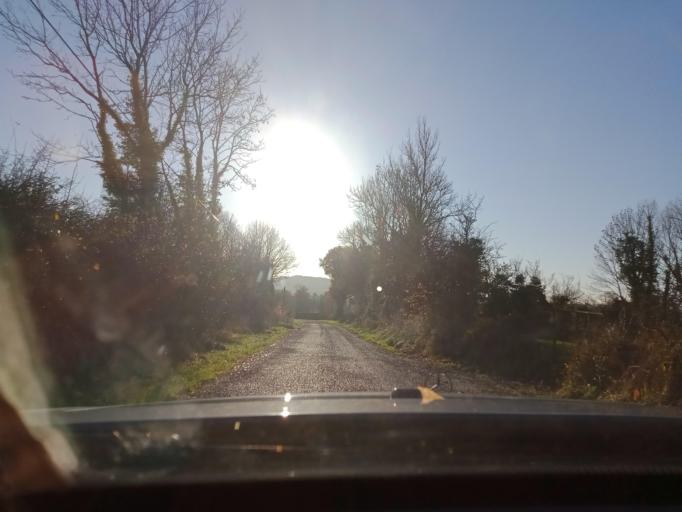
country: IE
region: Munster
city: Carrick-on-Suir
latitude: 52.4427
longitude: -7.4193
